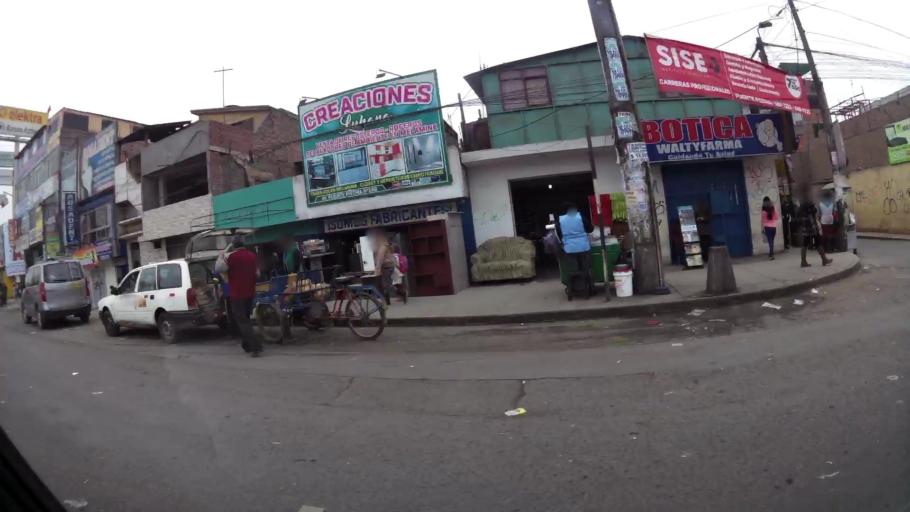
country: PE
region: Lima
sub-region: Lima
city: Carabayllo
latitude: -11.8620
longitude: -77.0777
